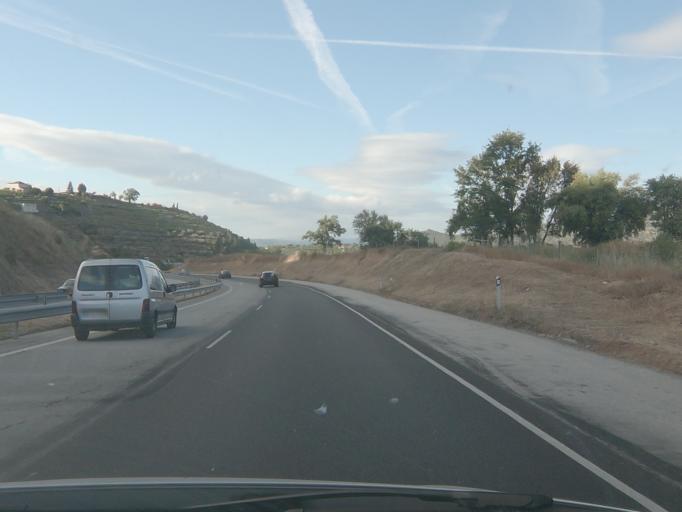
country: PT
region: Viseu
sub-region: Lamego
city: Lamego
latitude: 41.0920
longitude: -7.7829
